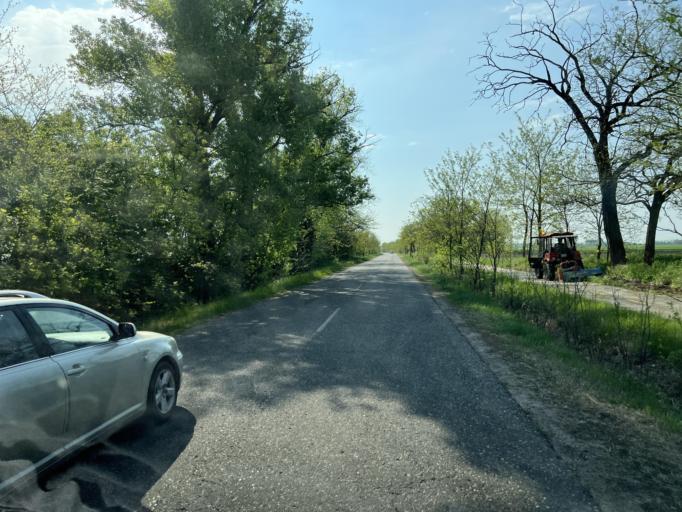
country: HU
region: Pest
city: Jaszkarajeno
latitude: 47.0868
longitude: 20.0338
